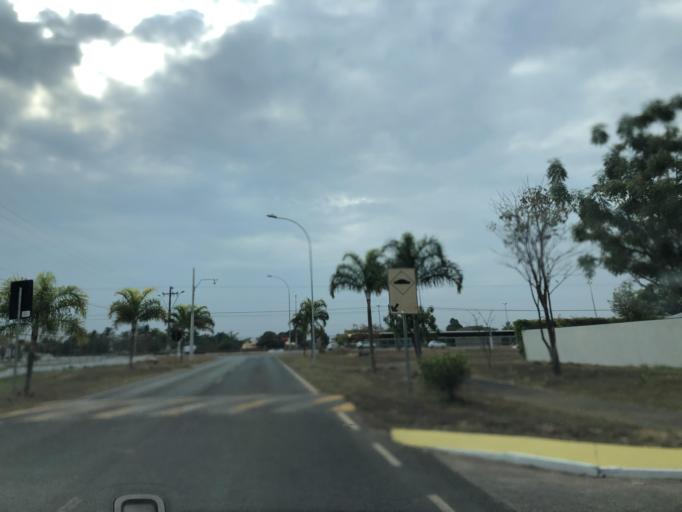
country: BR
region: Federal District
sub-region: Brasilia
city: Brasilia
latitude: -15.9436
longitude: -47.9873
